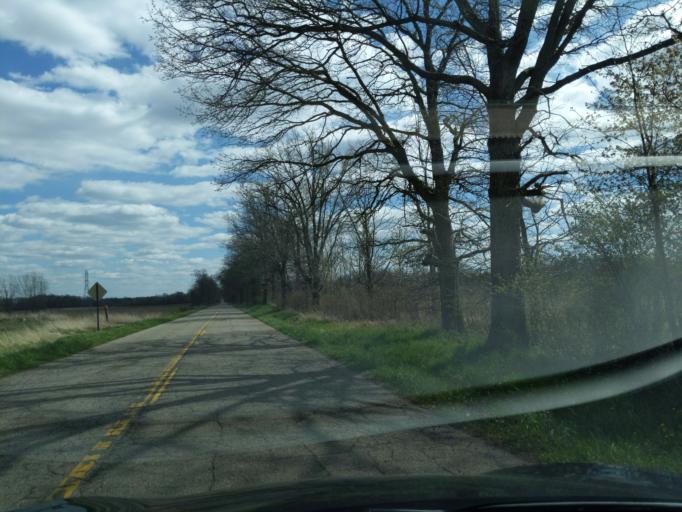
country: US
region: Michigan
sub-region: Ingham County
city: Leslie
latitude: 42.4211
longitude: -84.5267
